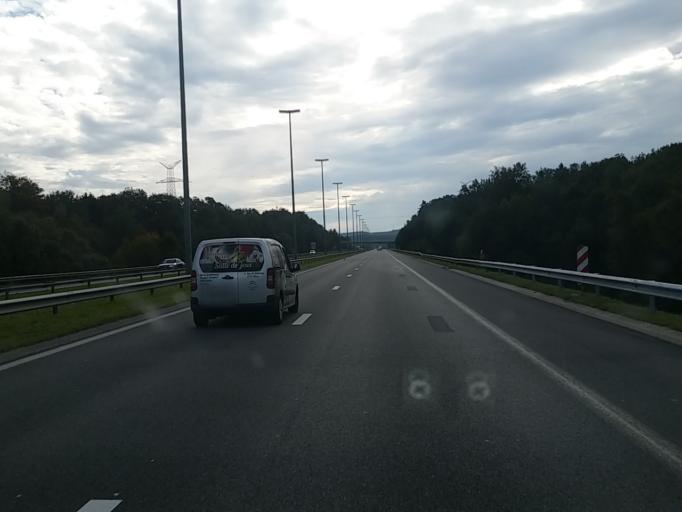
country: BE
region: Wallonia
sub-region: Province du Luxembourg
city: Arlon
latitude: 49.6831
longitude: 5.7540
